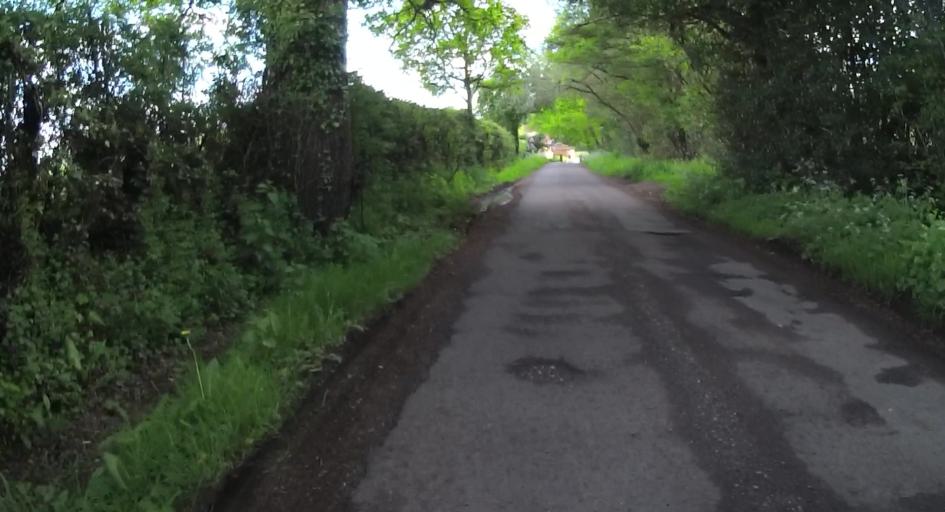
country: GB
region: England
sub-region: West Berkshire
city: Stratfield Mortimer
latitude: 51.3514
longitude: -1.0658
